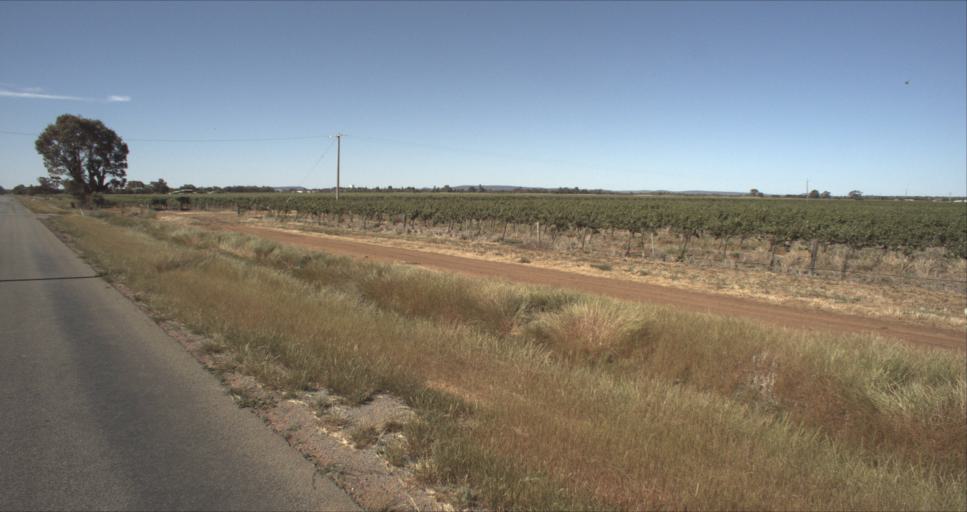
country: AU
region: New South Wales
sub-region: Leeton
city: Leeton
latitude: -34.5791
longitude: 146.3802
